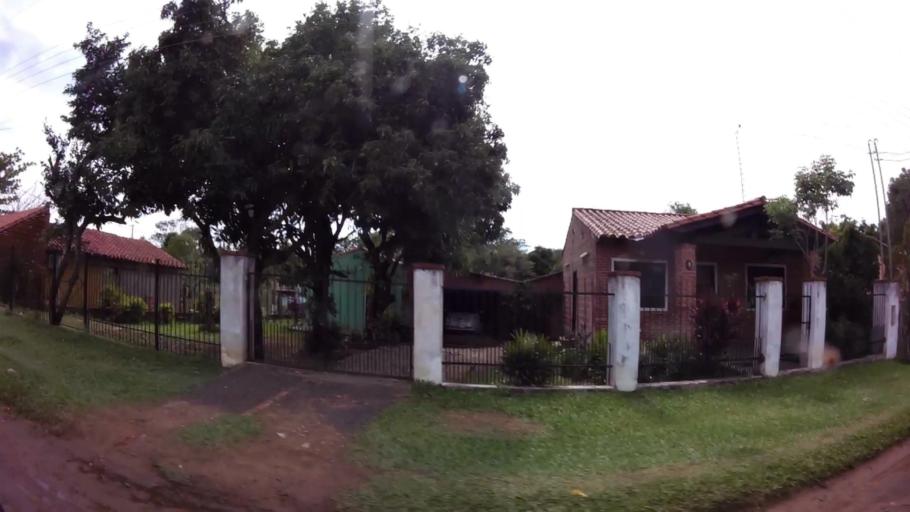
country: PY
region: Central
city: Limpio
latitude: -25.1280
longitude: -57.4750
